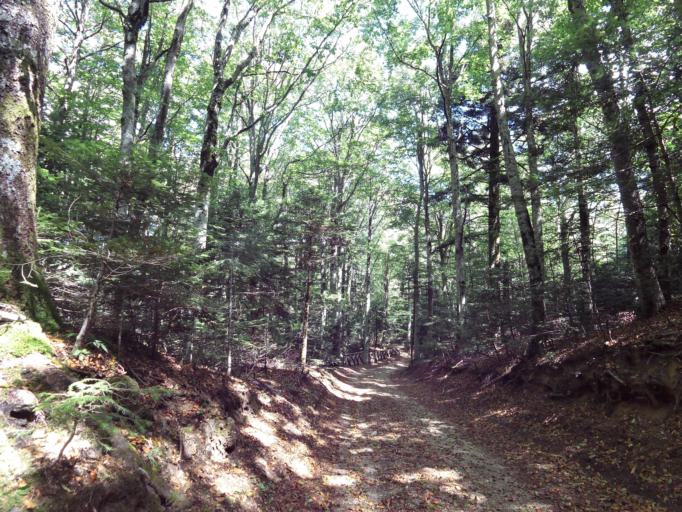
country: IT
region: Calabria
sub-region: Provincia di Vibo-Valentia
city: Mongiana
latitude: 38.5257
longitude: 16.3463
